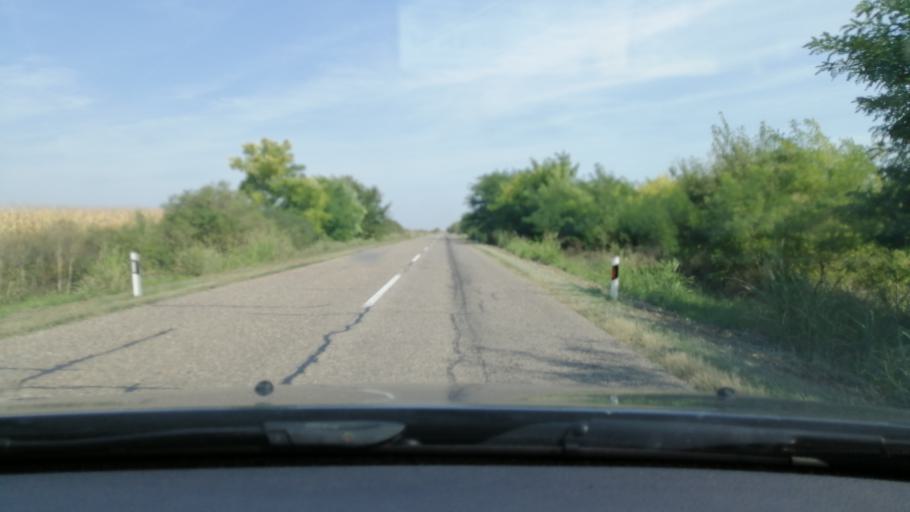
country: RS
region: Autonomna Pokrajina Vojvodina
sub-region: Juznobanatski Okrug
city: Kovacica
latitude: 45.1412
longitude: 20.6164
